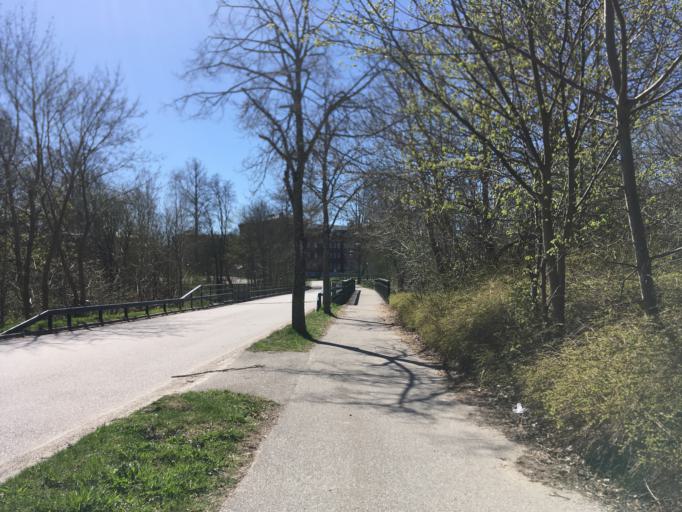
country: SE
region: Skane
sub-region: Lunds Kommun
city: Lund
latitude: 55.6848
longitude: 13.1800
